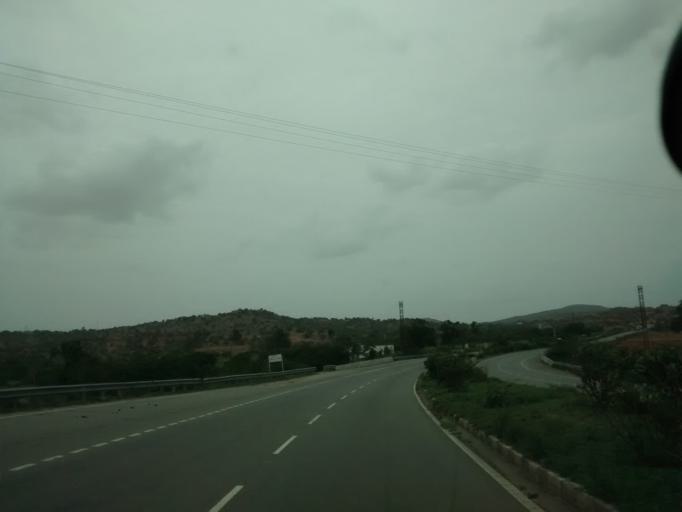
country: IN
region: Andhra Pradesh
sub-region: Kurnool
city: Ramapuram
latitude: 15.1963
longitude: 77.7031
